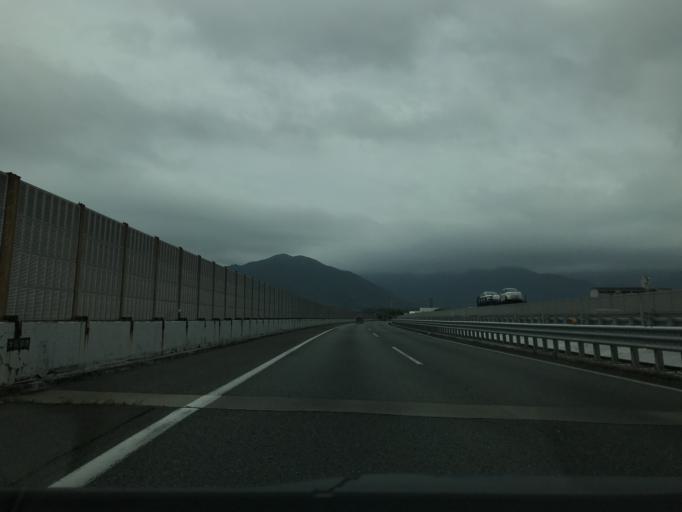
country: JP
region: Fukuoka
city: Nakama
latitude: 33.7833
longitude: 130.7218
